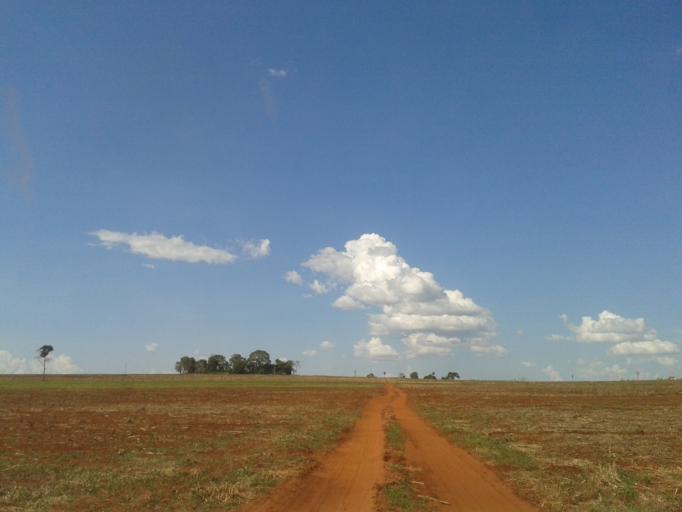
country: BR
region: Minas Gerais
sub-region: Santa Vitoria
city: Santa Vitoria
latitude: -19.1093
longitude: -50.3933
